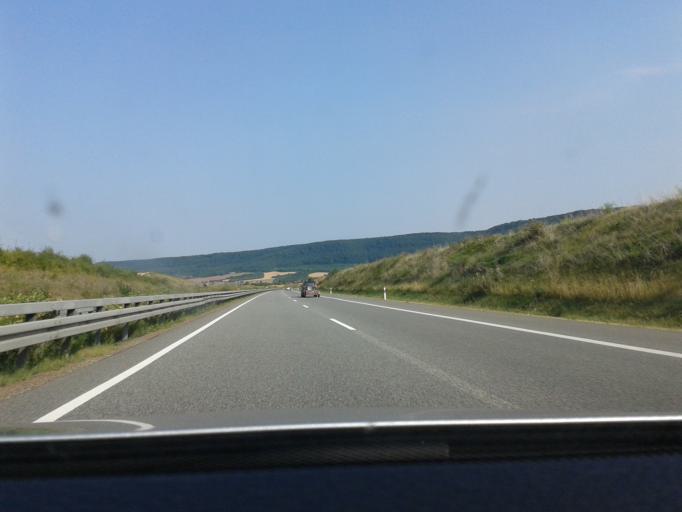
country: DE
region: Thuringia
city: Sollstedt
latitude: 51.4201
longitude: 10.5478
